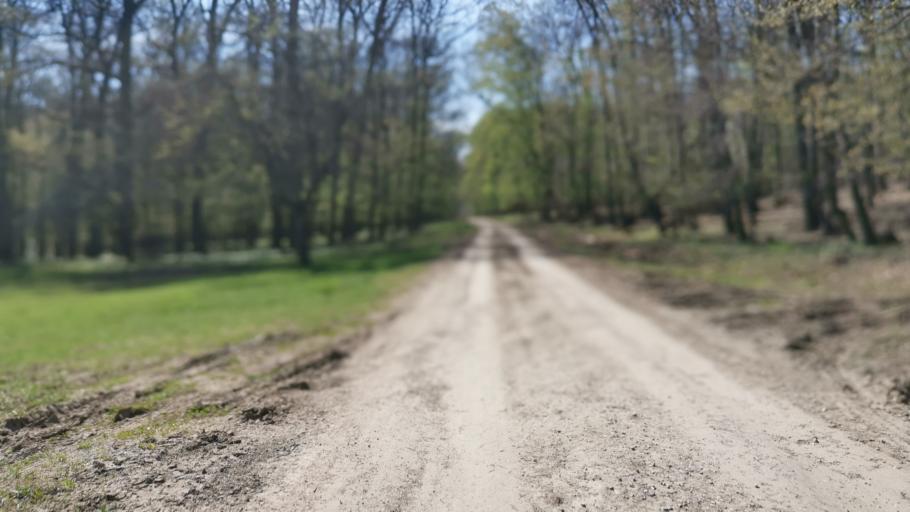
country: SK
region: Trnavsky
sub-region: Okres Skalica
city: Holic
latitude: 48.7383
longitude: 17.2250
